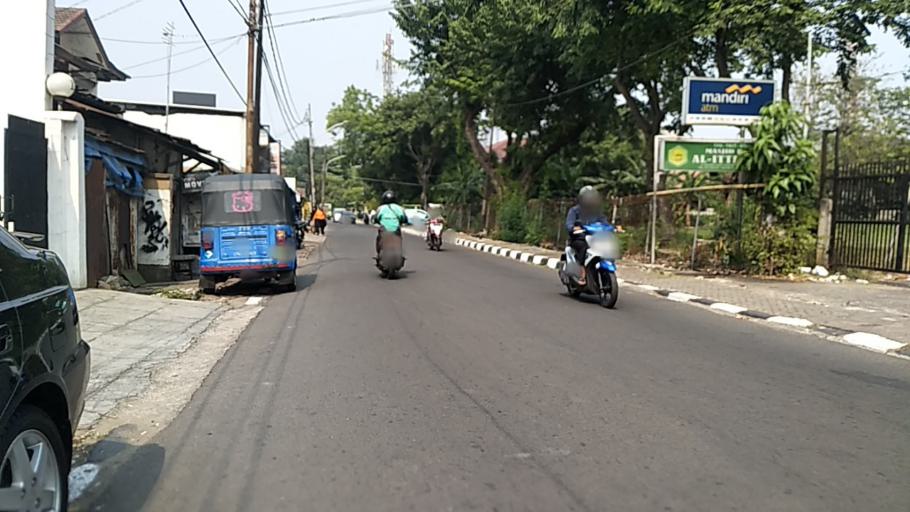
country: ID
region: Jakarta Raya
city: Jakarta
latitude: -6.2318
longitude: 106.8493
